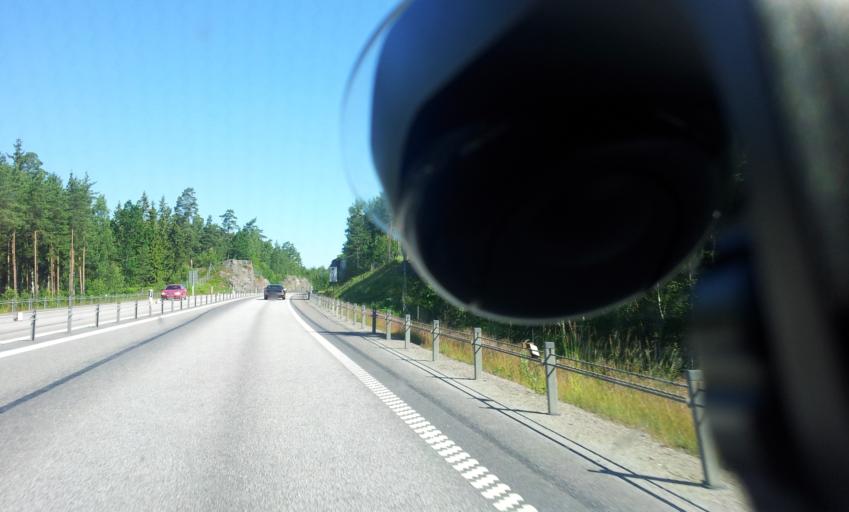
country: SE
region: OEstergoetland
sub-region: Valdemarsviks Kommun
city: Gusum
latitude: 58.3456
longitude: 16.4484
